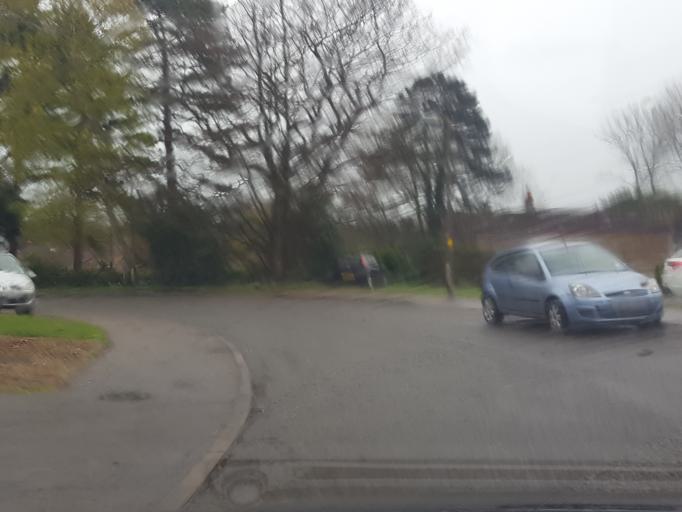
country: GB
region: England
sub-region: Essex
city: Great Horkesley
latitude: 51.9243
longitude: 0.8810
